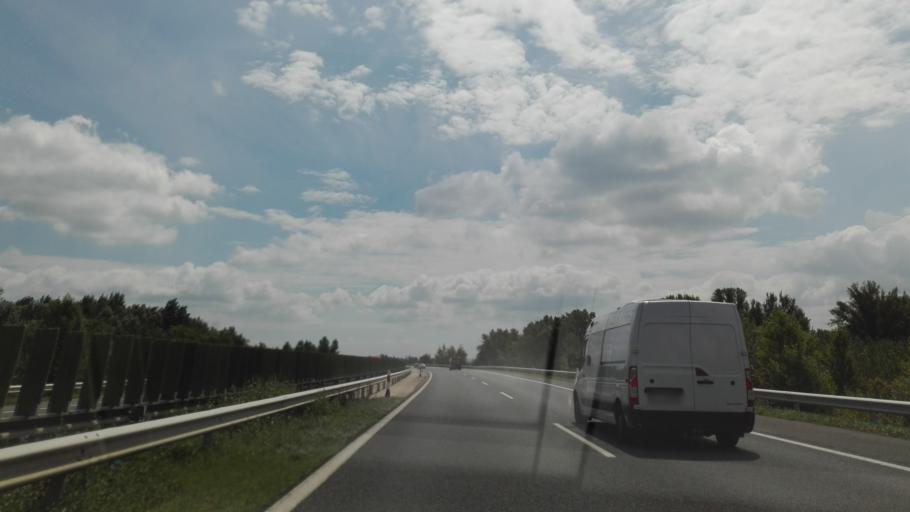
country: HU
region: Gyor-Moson-Sopron
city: Abda
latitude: 47.6817
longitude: 17.5417
